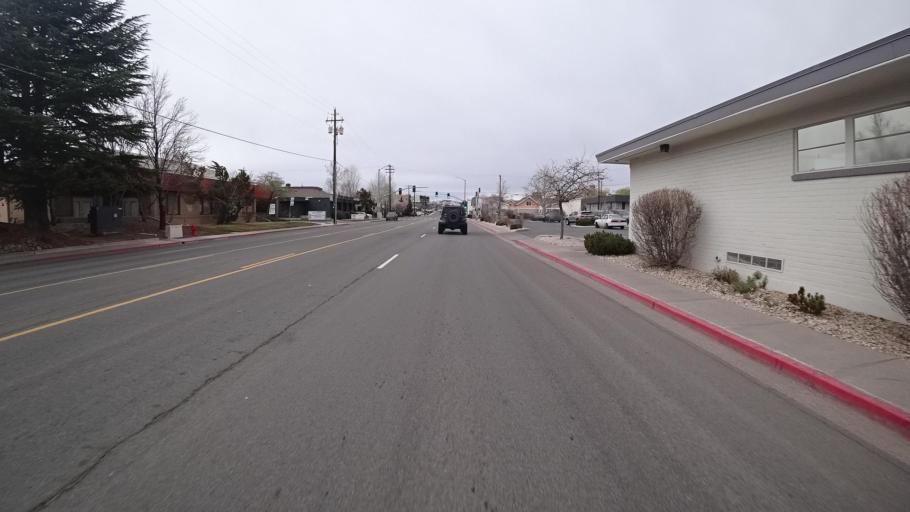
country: US
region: Nevada
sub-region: Washoe County
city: Reno
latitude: 39.5239
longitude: -119.7994
